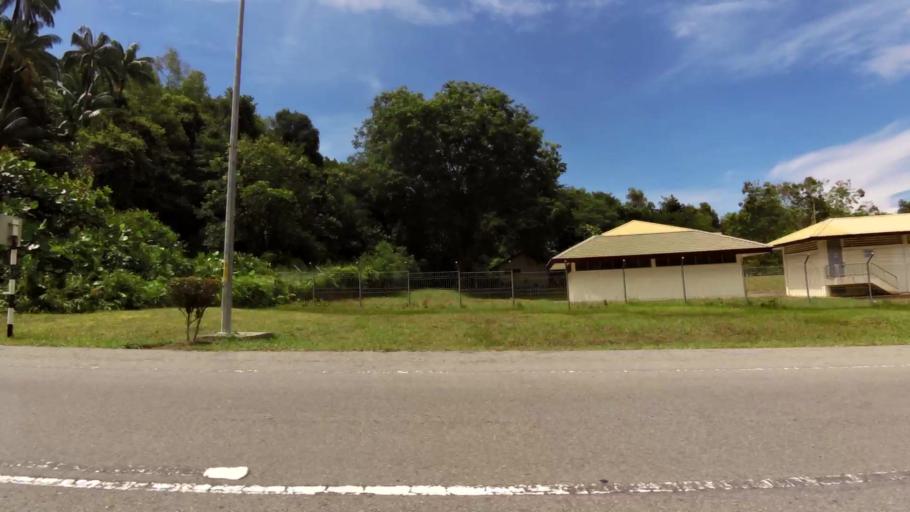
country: BN
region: Brunei and Muara
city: Bandar Seri Begawan
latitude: 4.9958
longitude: 114.9441
